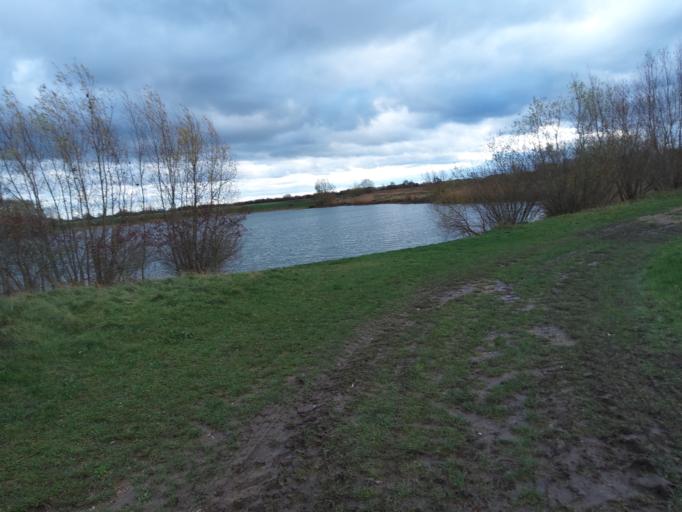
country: NL
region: Gelderland
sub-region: Gemeente Neerijnen
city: Neerijnen
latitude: 51.8275
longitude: 5.2655
